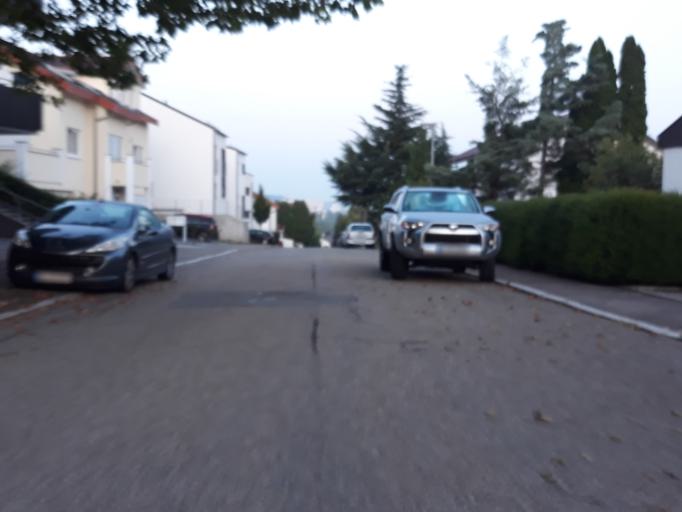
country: DE
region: Baden-Wuerttemberg
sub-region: Regierungsbezirk Stuttgart
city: Boeblingen
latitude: 48.6799
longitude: 9.0313
